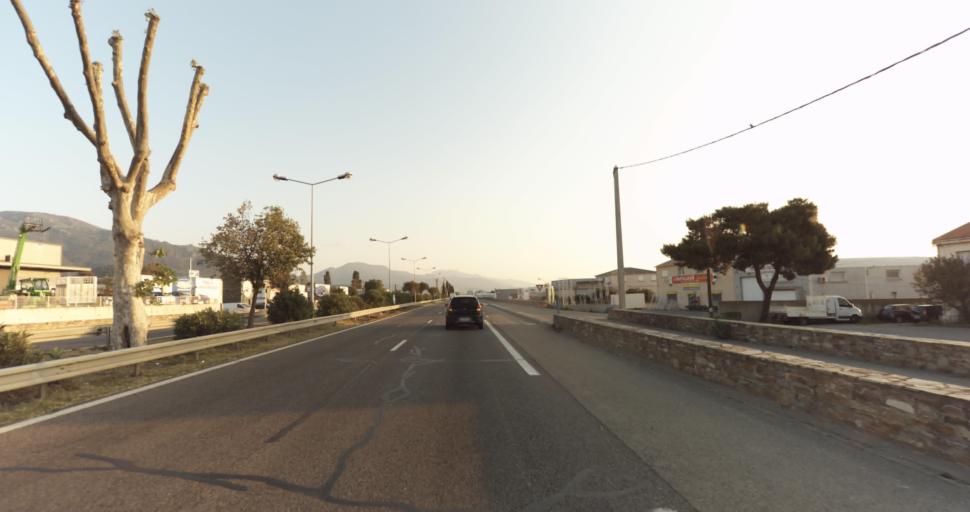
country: FR
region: Corsica
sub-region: Departement de la Haute-Corse
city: Biguglia
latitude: 42.5898
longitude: 9.4393
